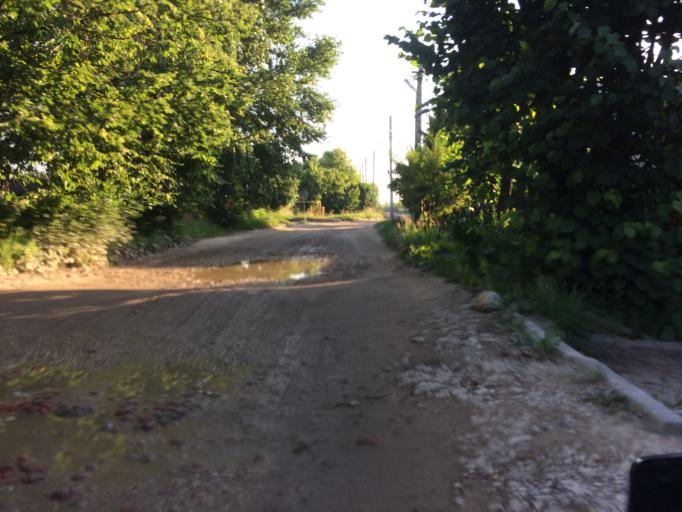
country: RU
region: Mariy-El
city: Yoshkar-Ola
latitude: 56.6540
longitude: 47.8863
